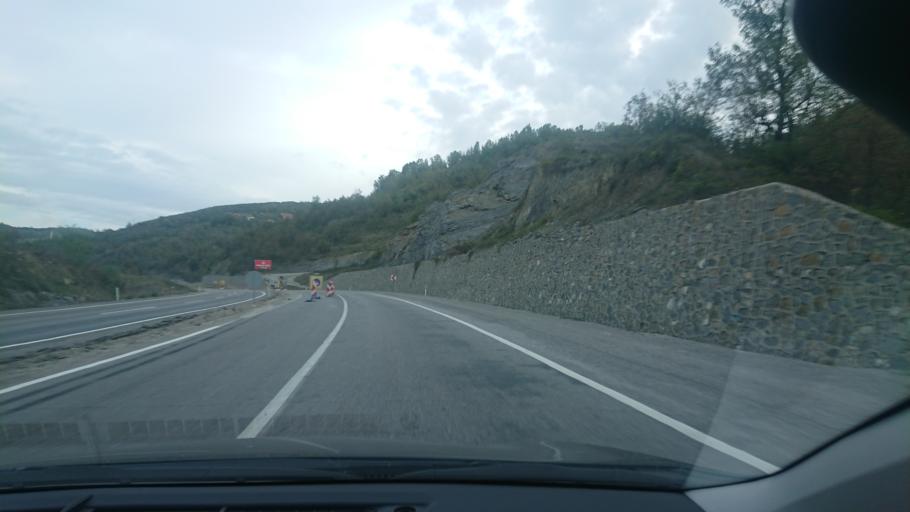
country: TR
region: Zonguldak
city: Beycuma
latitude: 41.3995
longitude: 31.9376
